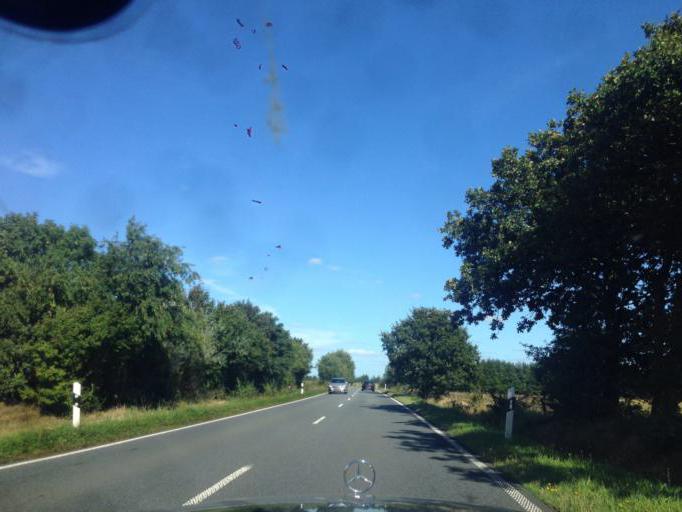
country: DE
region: Schleswig-Holstein
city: Nordhackstedt
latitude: 54.7556
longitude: 9.1443
